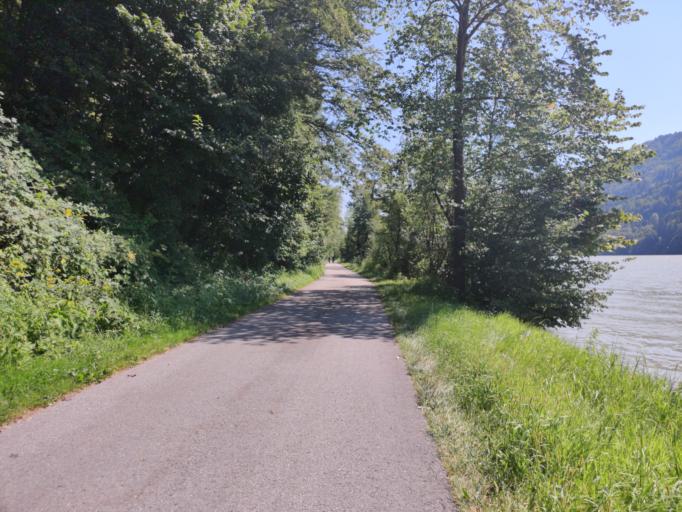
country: AT
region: Upper Austria
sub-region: Politischer Bezirk Rohrbach
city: Pfarrkirchen im Muehlkreis
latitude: 48.4378
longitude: 13.8453
